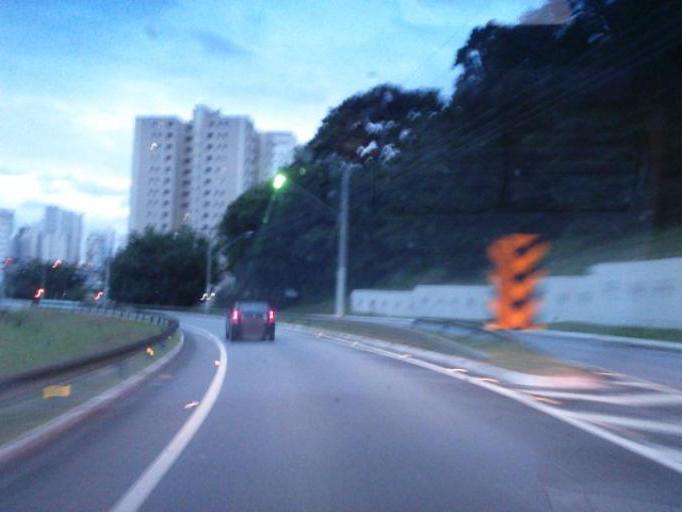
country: BR
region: Sao Paulo
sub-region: Sao Jose Dos Campos
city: Sao Jose dos Campos
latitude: -23.2089
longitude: -45.8970
